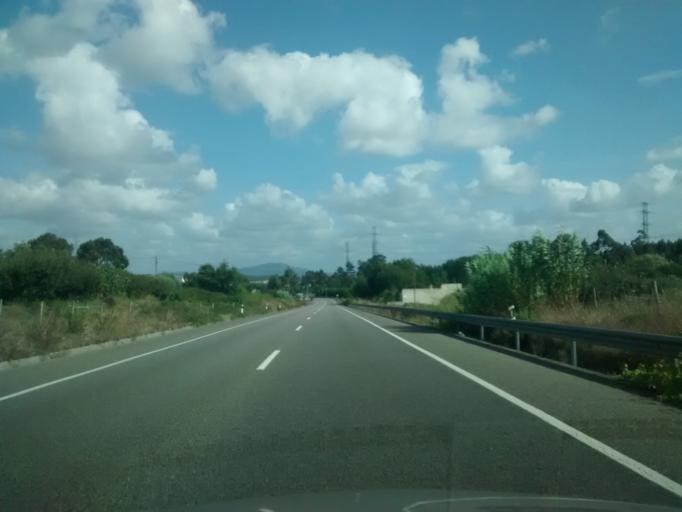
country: PT
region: Aveiro
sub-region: Anadia
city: Sangalhos
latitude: 40.4716
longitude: -8.4699
